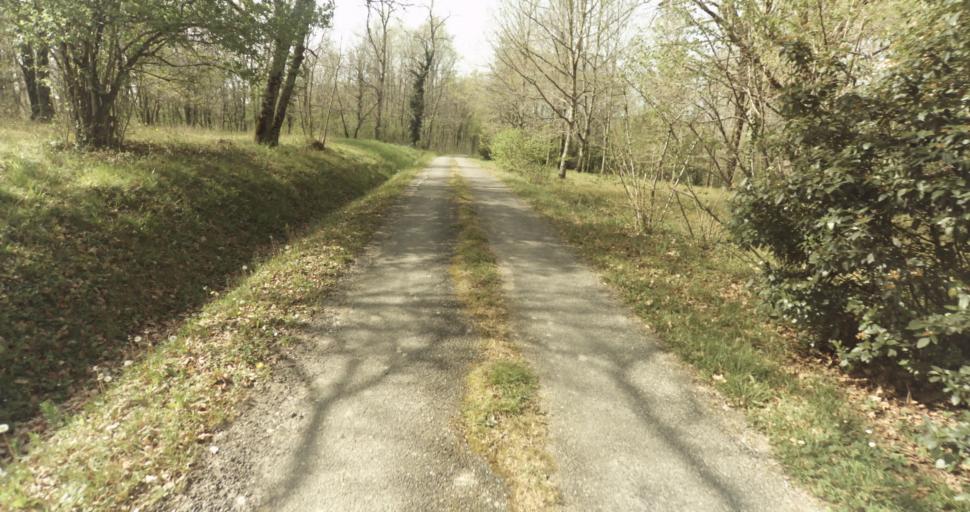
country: FR
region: Midi-Pyrenees
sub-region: Departement du Tarn-et-Garonne
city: Lafrancaise
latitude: 44.1501
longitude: 1.1788
